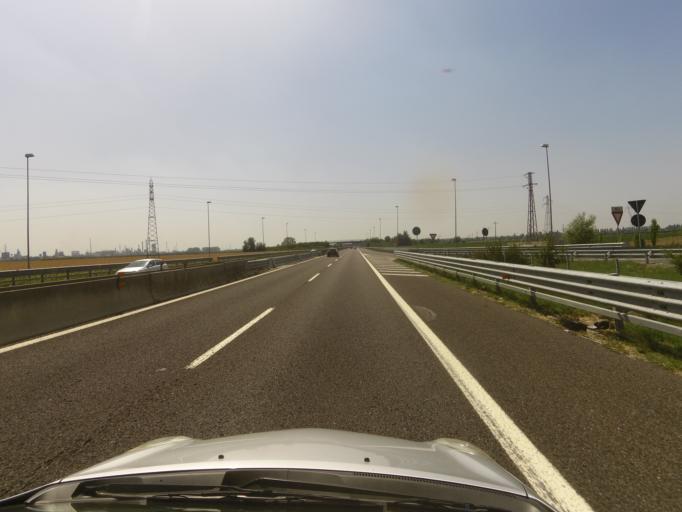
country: IT
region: Emilia-Romagna
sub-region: Provincia di Ferrara
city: Porotto-Cassama
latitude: 44.8782
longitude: 11.5699
